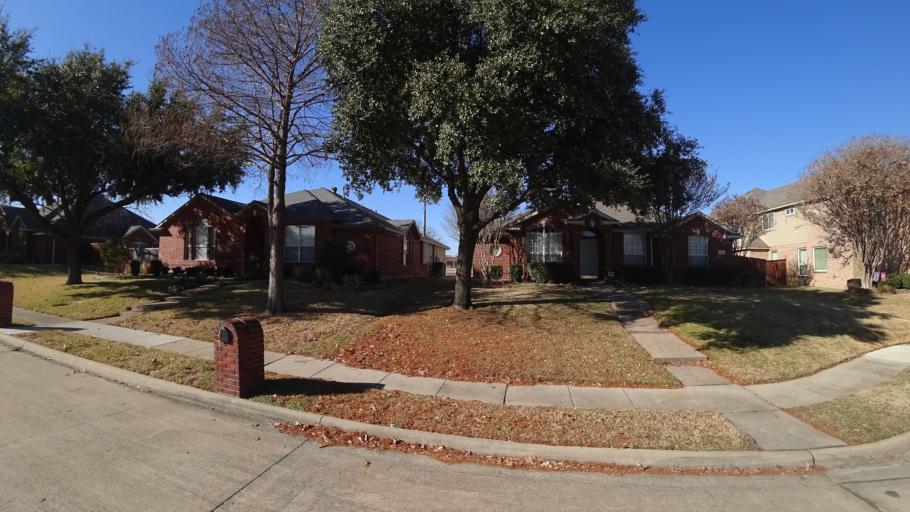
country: US
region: Texas
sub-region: Denton County
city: Lewisville
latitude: 33.0163
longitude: -97.0330
